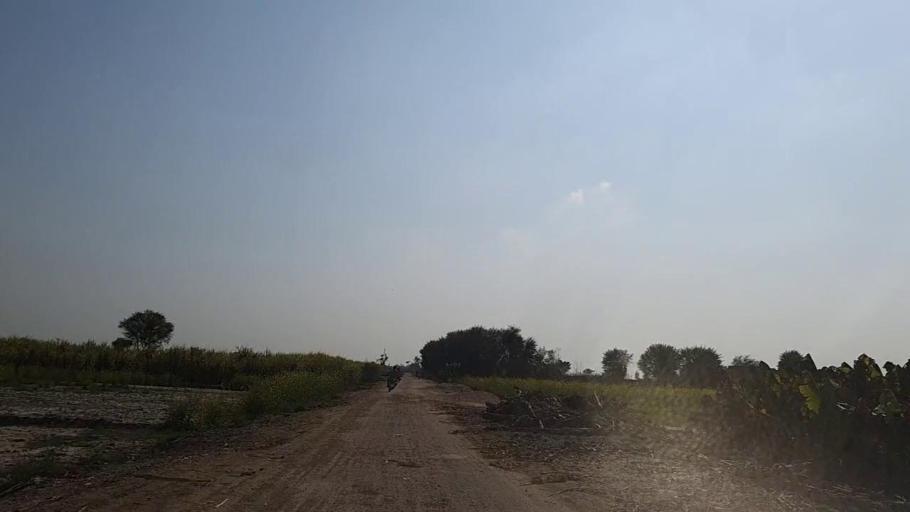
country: PK
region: Sindh
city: Daur
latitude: 26.4201
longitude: 68.2368
